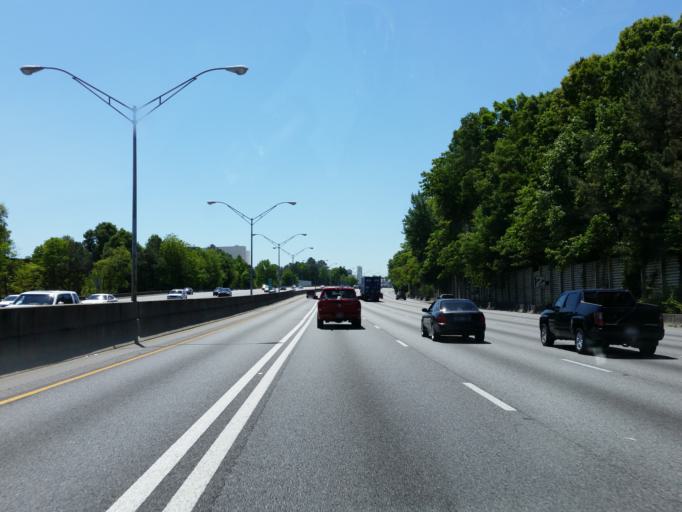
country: US
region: Georgia
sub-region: Fulton County
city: Hapeville
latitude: 33.6645
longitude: -84.3962
